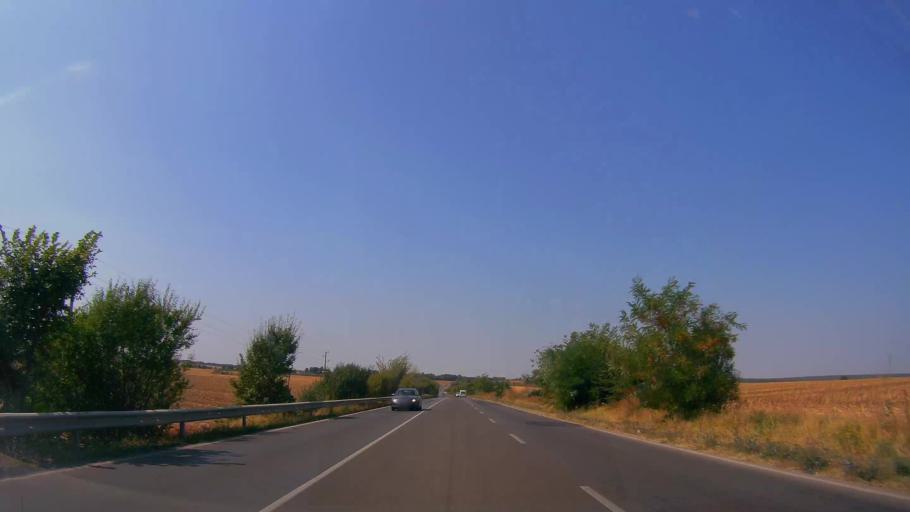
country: BG
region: Ruse
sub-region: Obshtina Vetovo
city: Senovo
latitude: 43.5657
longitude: 26.3329
